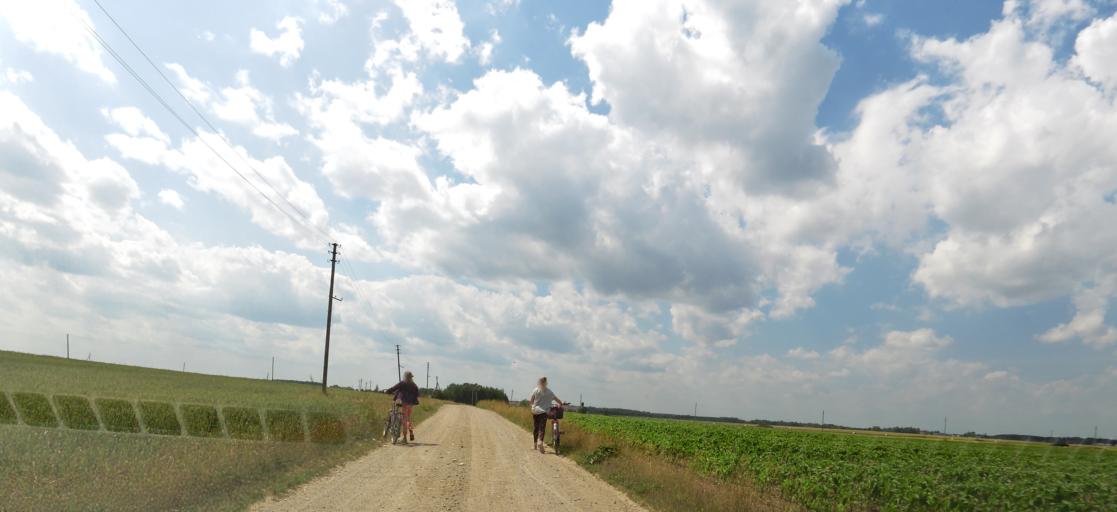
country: LT
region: Panevezys
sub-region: Birzai
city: Birzai
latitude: 56.1206
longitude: 24.8945
